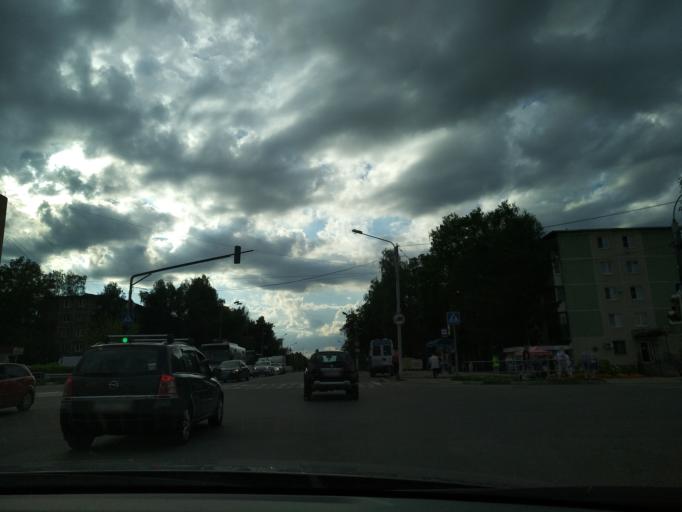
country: RU
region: Moskovskaya
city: Yegor'yevsk
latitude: 55.3690
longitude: 39.0669
